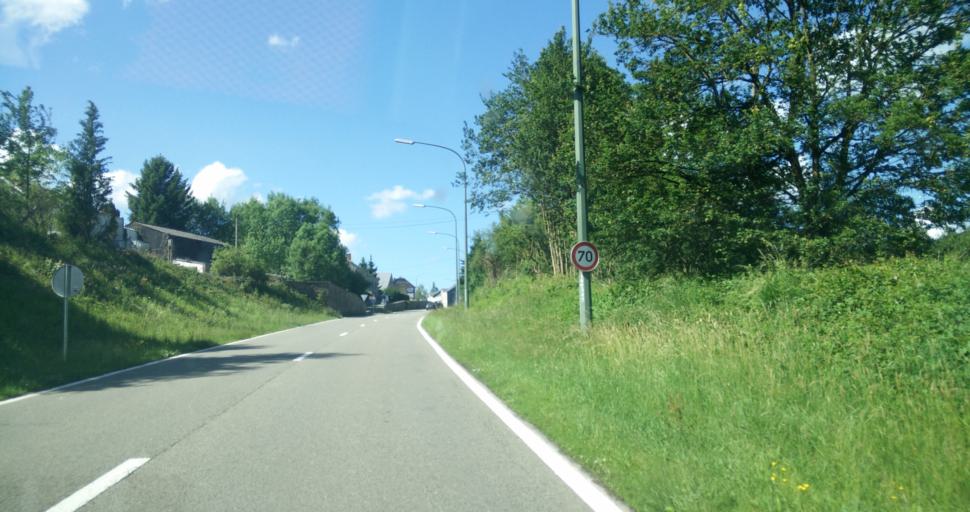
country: BE
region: Wallonia
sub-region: Province du Luxembourg
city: Marche-en-Famenne
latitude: 50.2068
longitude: 5.3680
